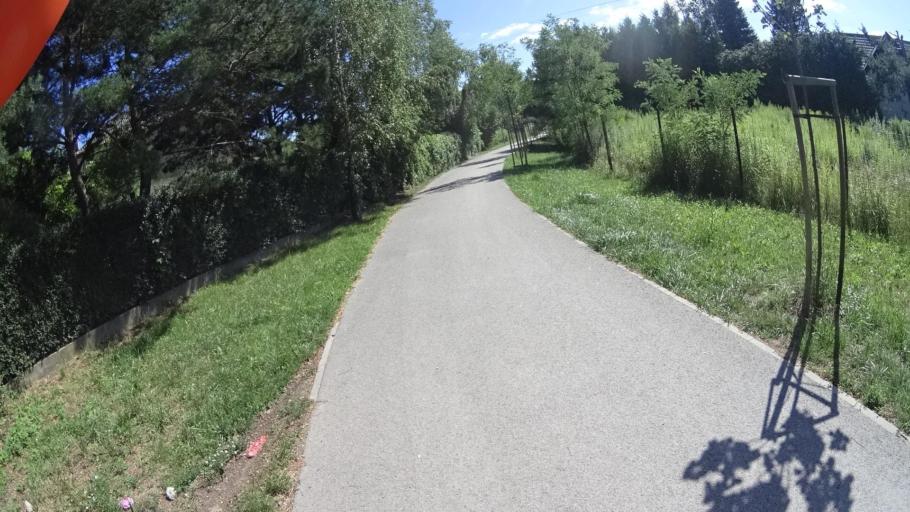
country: PL
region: Masovian Voivodeship
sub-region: Powiat piaseczynski
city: Jozefoslaw
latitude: 52.1064
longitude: 21.0556
